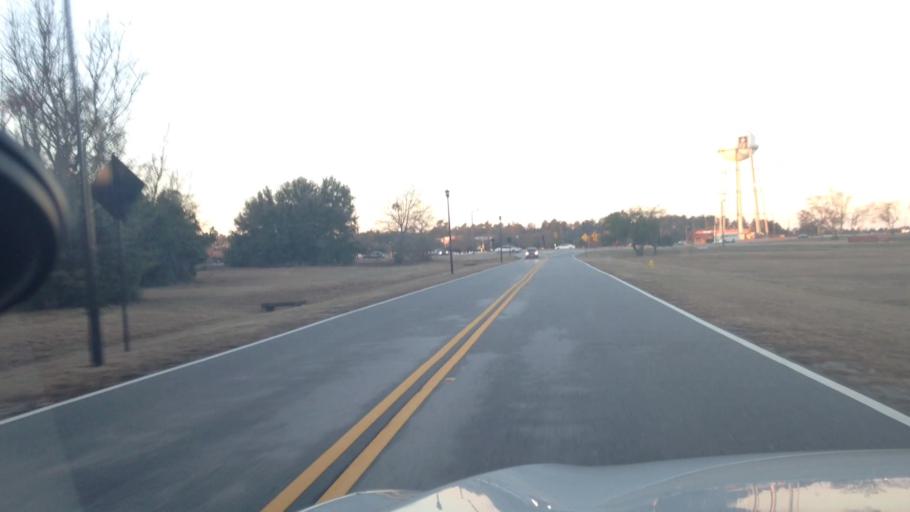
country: US
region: Georgia
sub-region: Columbia County
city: Grovetown
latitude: 33.4171
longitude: -82.1362
